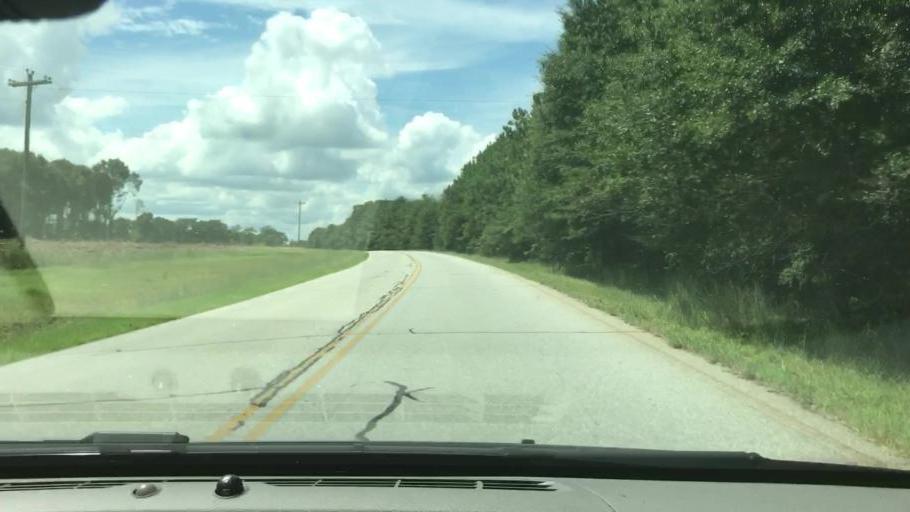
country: US
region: Georgia
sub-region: Stewart County
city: Lumpkin
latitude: 32.1383
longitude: -84.9704
